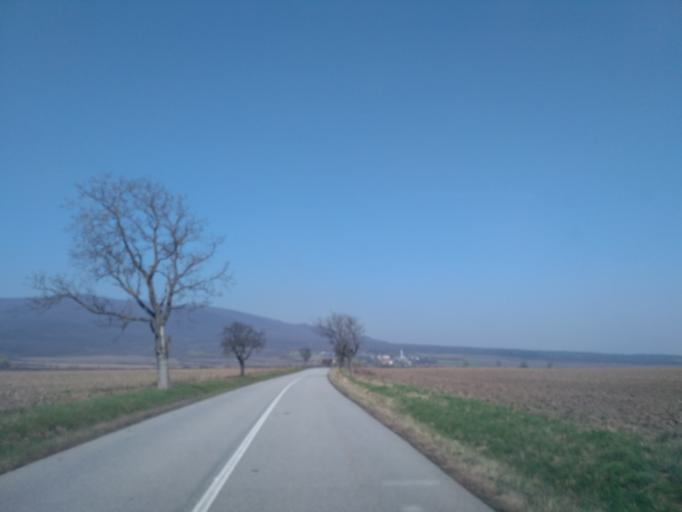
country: SK
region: Kosicky
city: Secovce
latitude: 48.7426
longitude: 21.6466
